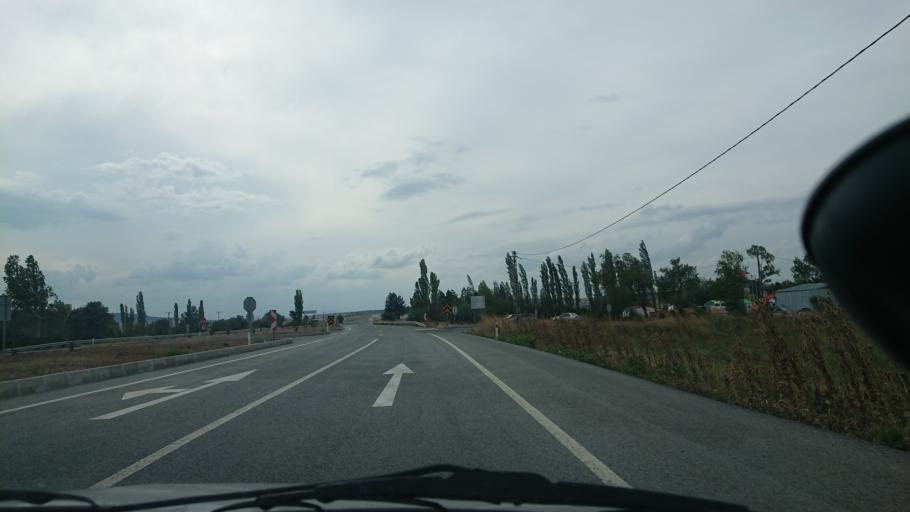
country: TR
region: Kuetahya
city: Aslanapa
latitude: 39.2519
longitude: 29.8434
